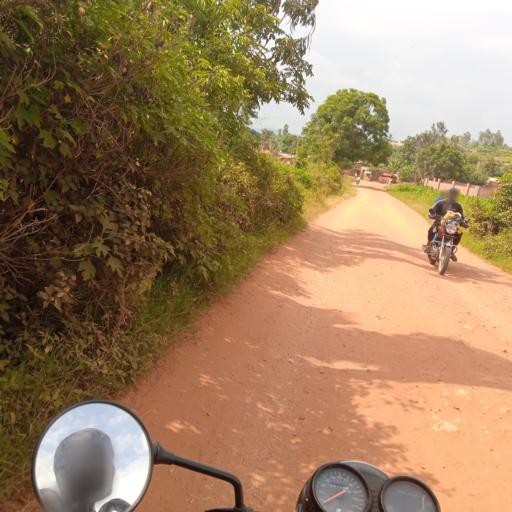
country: UG
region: Eastern Region
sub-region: Mbale District
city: Mbale
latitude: 1.0954
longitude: 34.1899
